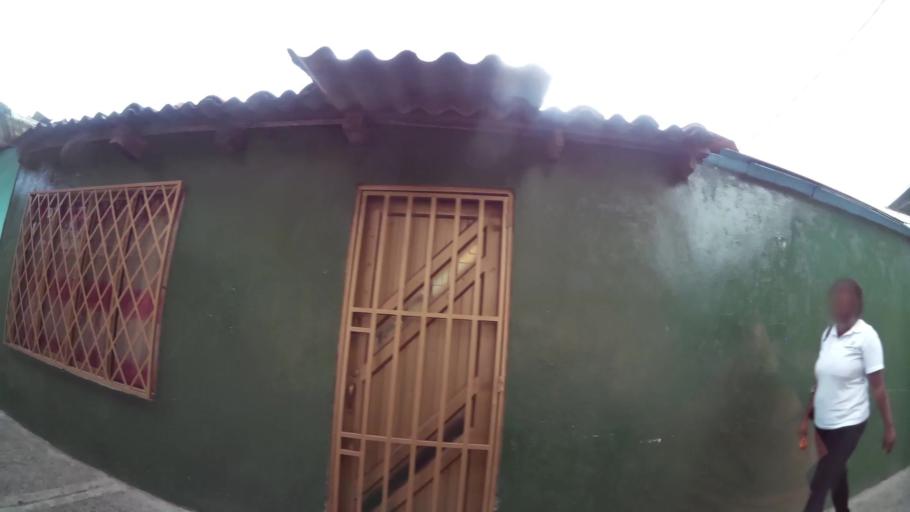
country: CO
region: Valle del Cauca
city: Cali
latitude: 3.4606
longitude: -76.4873
